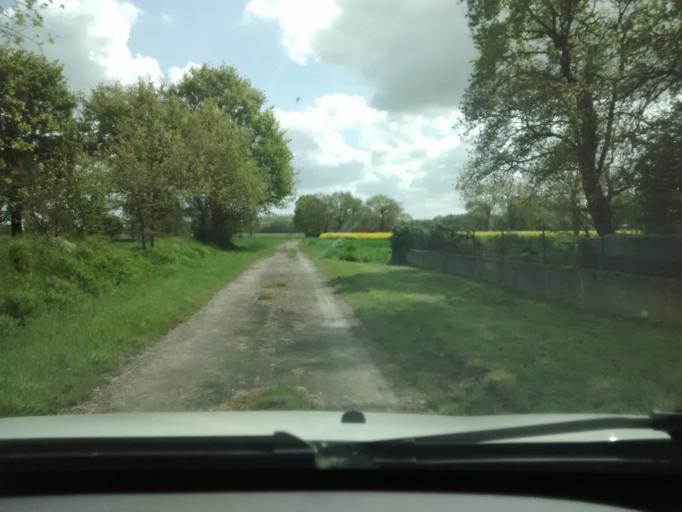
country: FR
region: Brittany
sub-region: Departement d'Ille-et-Vilaine
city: Chantepie
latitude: 48.0922
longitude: -1.5814
